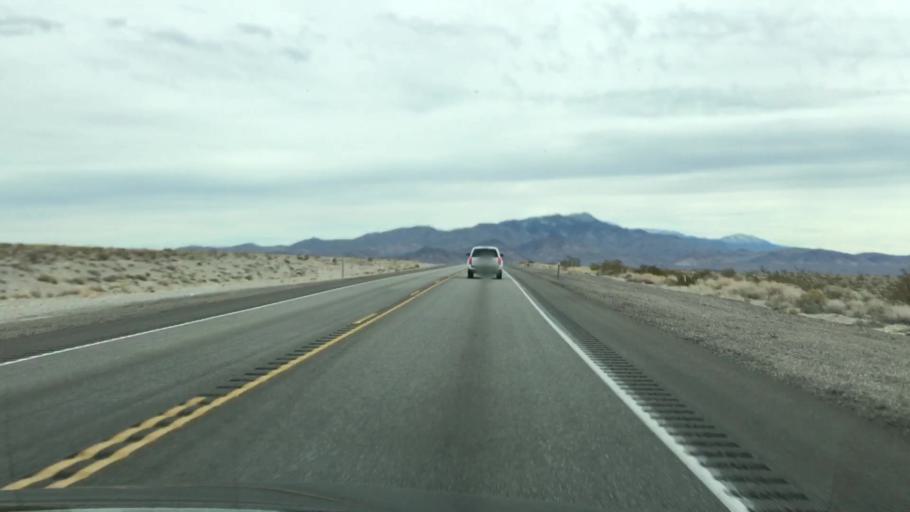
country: US
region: Nevada
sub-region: Nye County
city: Pahrump
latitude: 36.5783
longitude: -116.1966
